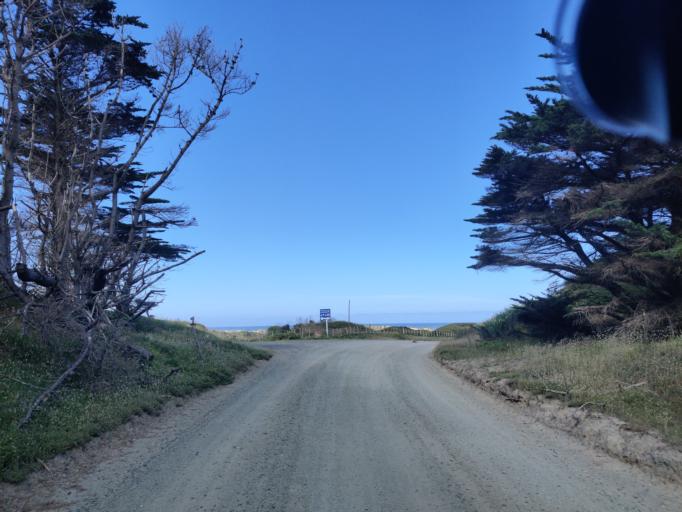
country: NZ
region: Northland
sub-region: Far North District
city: Kaitaia
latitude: -34.8981
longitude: 173.0916
